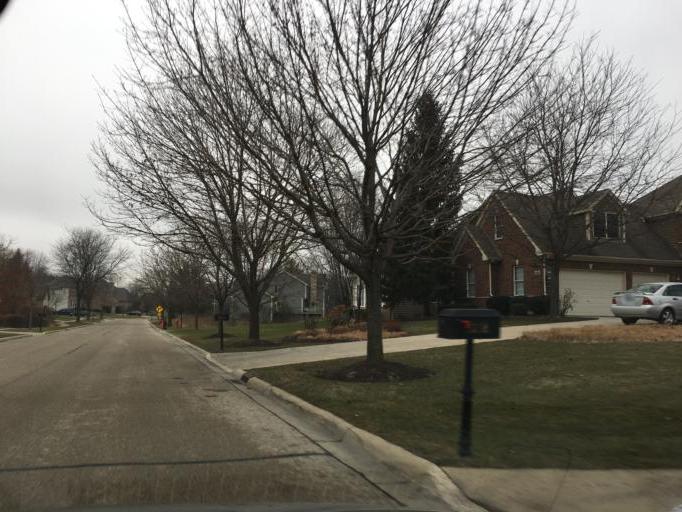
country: US
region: Illinois
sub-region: McHenry County
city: Lakewood
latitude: 42.2195
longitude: -88.3584
